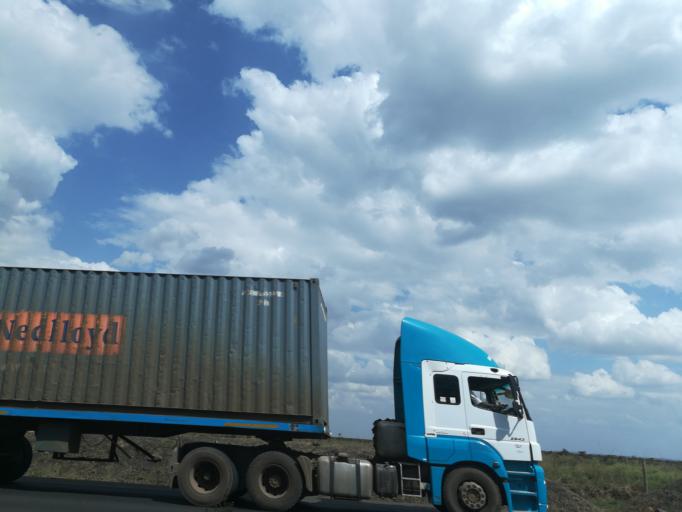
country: KE
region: Nairobi Area
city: Nairobi
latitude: -1.3302
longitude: 36.8303
